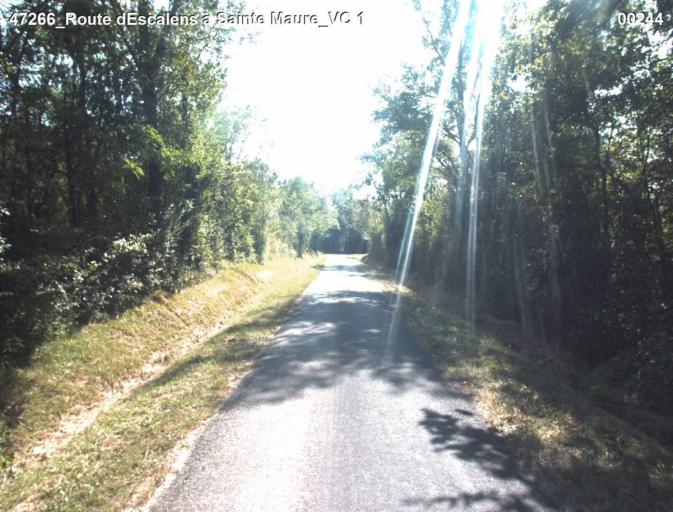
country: FR
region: Aquitaine
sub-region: Departement des Landes
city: Gabarret
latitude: 44.0097
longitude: 0.0633
